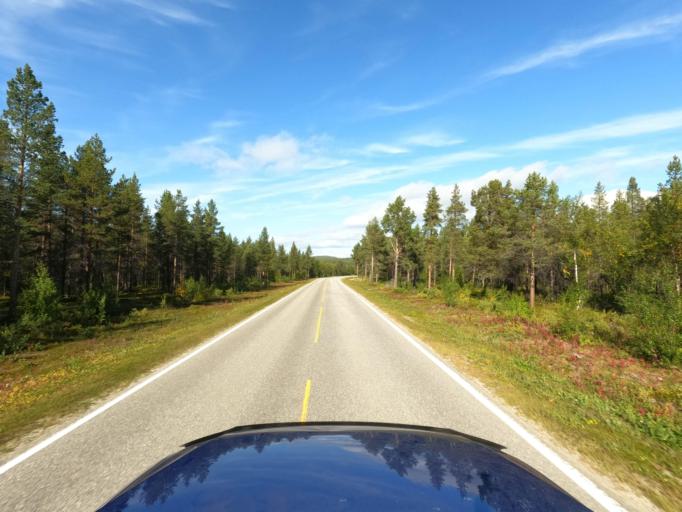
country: NO
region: Finnmark Fylke
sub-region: Porsanger
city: Lakselv
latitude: 69.8161
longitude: 25.1582
